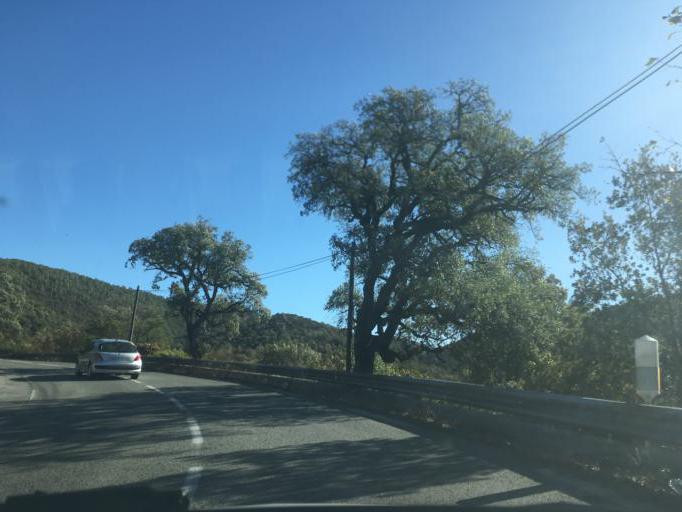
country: FR
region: Provence-Alpes-Cote d'Azur
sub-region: Departement du Var
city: La Garde-Freinet
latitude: 43.3313
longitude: 6.4398
